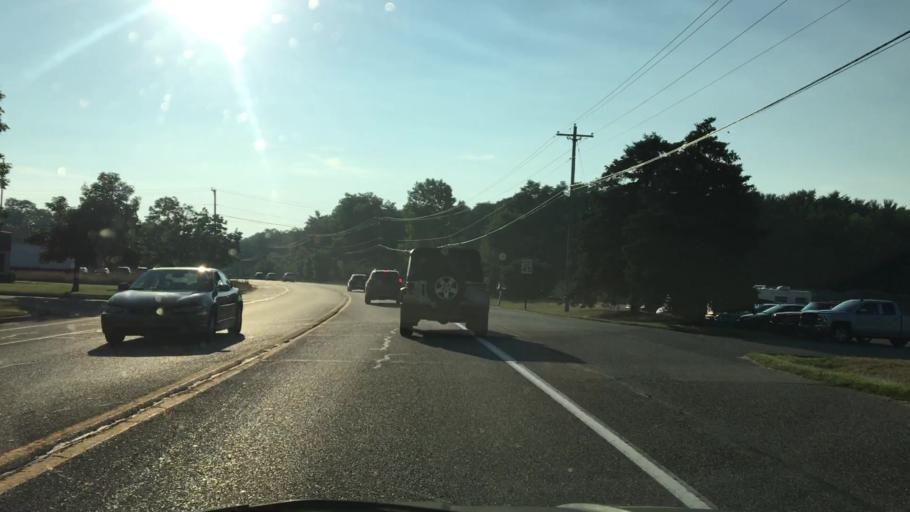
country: US
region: Michigan
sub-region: Livingston County
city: Brighton
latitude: 42.5154
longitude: -83.7161
